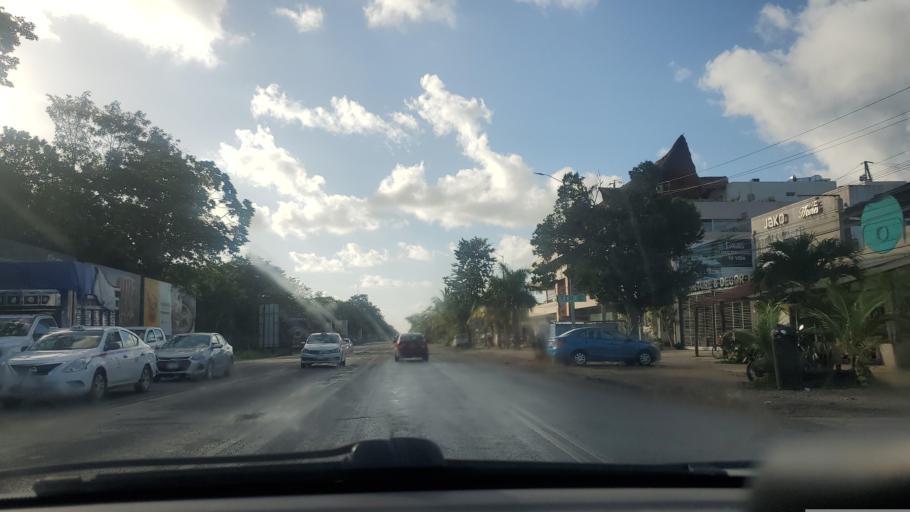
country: MX
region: Quintana Roo
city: Tulum
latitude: 20.2139
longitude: -87.4533
